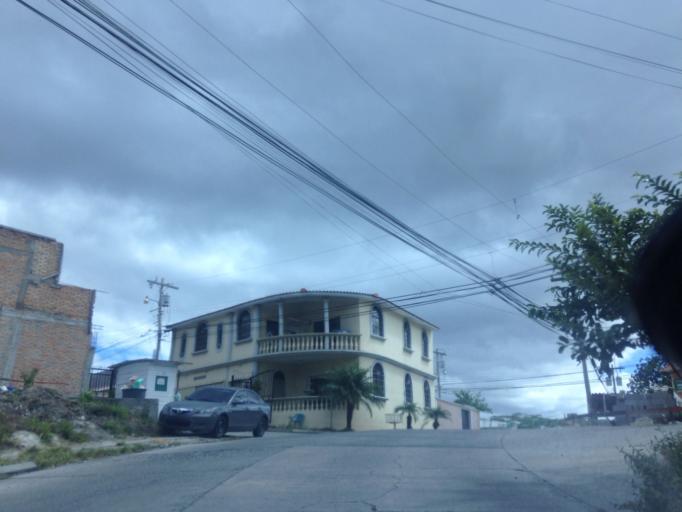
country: HN
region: Francisco Morazan
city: Tegucigalpa
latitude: 14.0547
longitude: -87.2395
